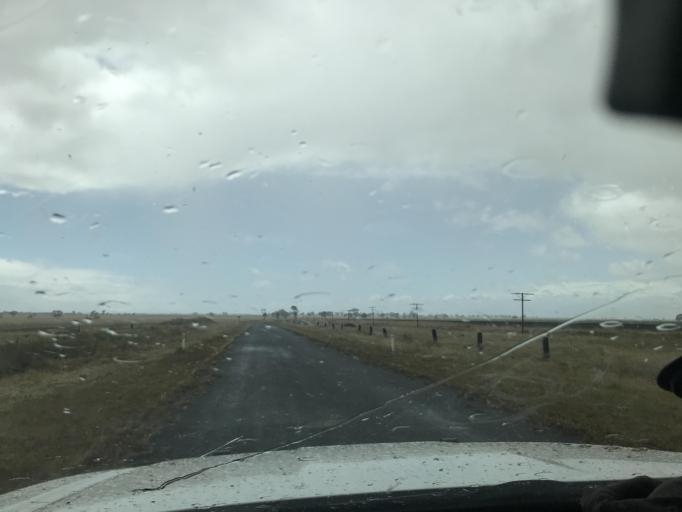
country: AU
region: South Australia
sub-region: Tatiara
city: Bordertown
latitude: -36.3750
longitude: 140.9935
